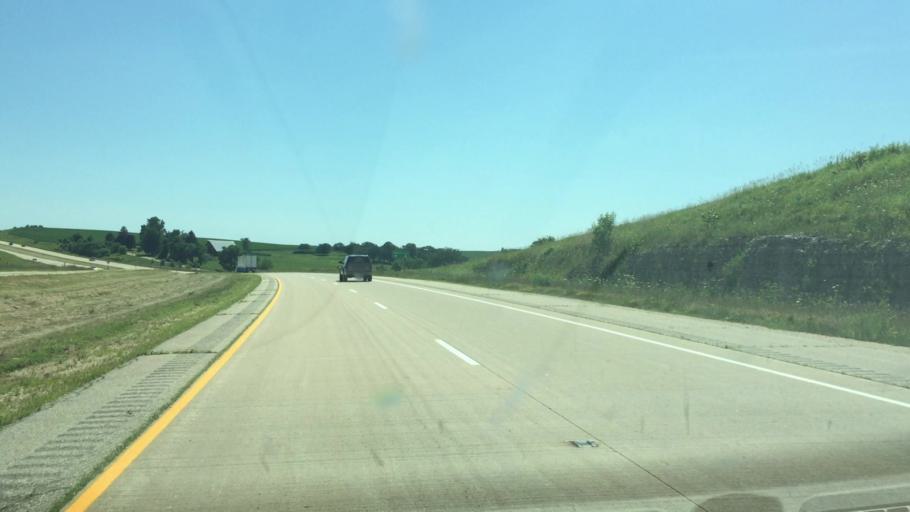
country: US
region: Wisconsin
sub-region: Iowa County
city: Mineral Point
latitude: 42.7760
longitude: -90.3109
